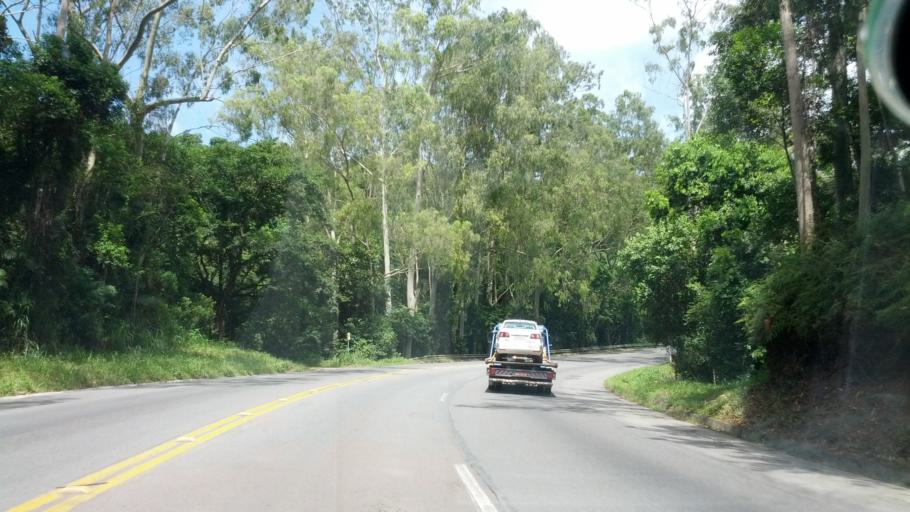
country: BR
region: Santa Catarina
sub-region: Ibirama
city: Ibirama
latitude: -27.0954
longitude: -49.5261
